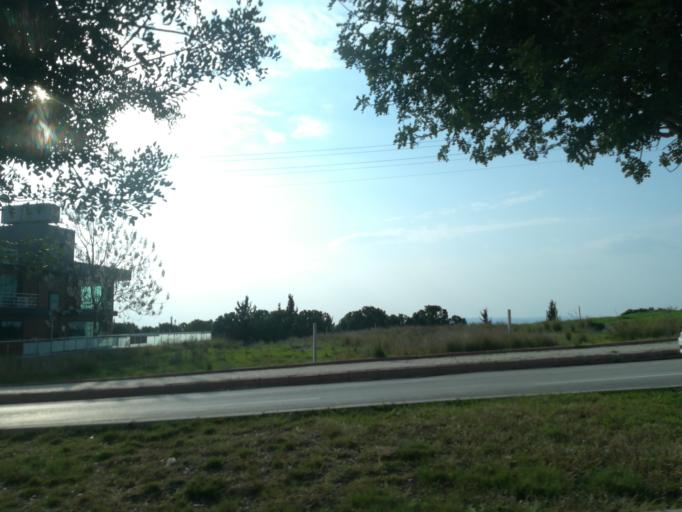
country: TR
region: Adana
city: Adana
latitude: 37.0769
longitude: 35.3884
